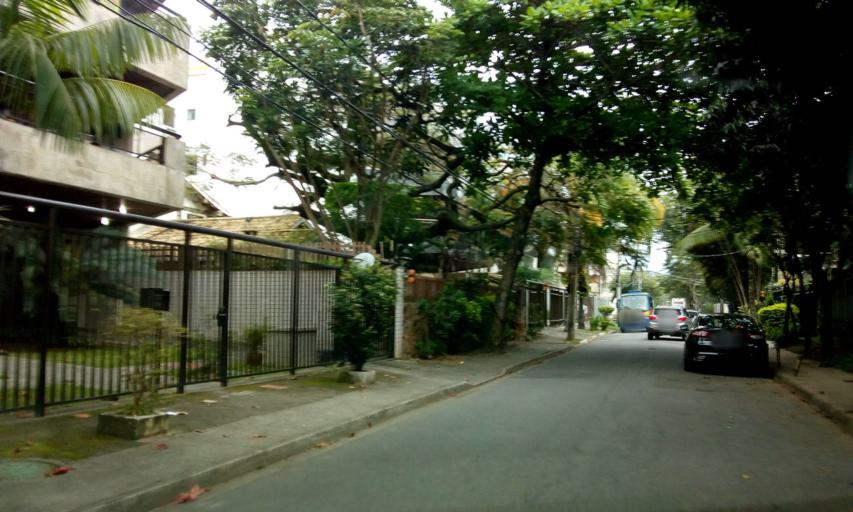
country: BR
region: Rio de Janeiro
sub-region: Nilopolis
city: Nilopolis
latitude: -23.0196
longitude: -43.4530
